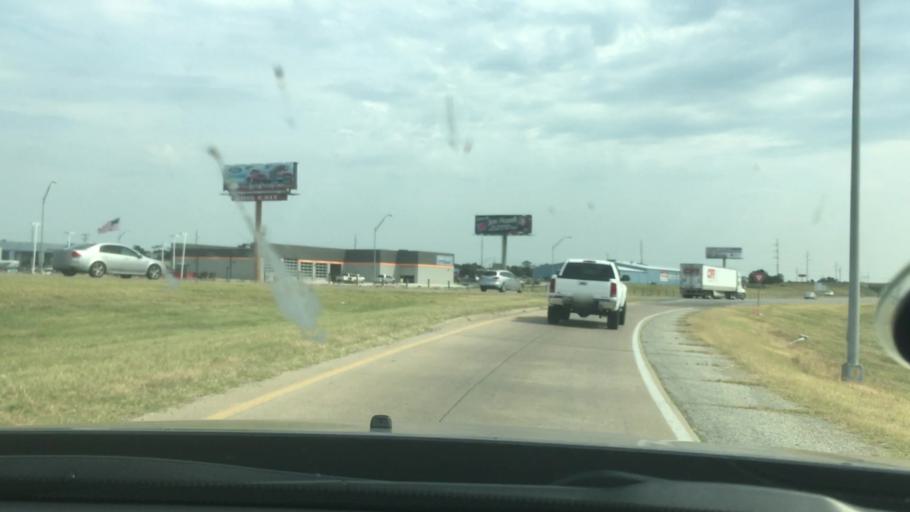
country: US
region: Oklahoma
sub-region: Bryan County
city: Durant
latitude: 33.9998
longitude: -96.4026
